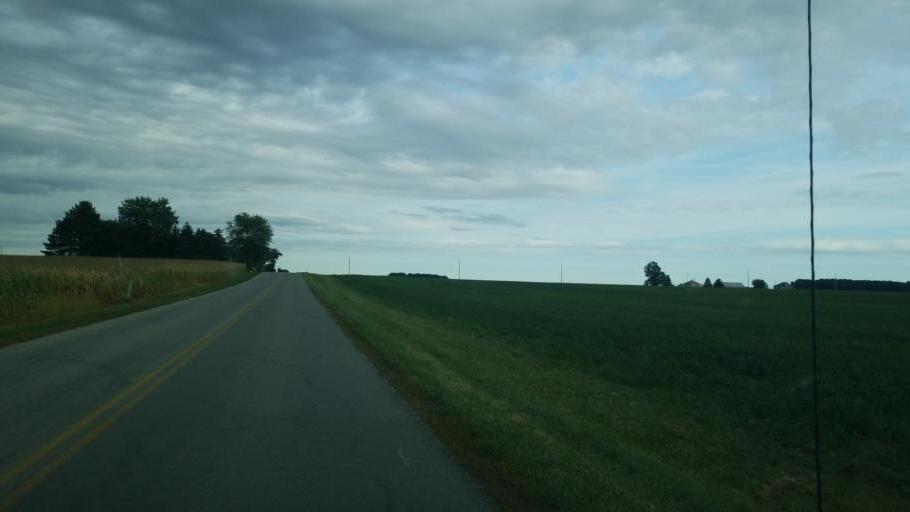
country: US
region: Ohio
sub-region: Wyandot County
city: Upper Sandusky
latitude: 40.9055
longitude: -83.3108
